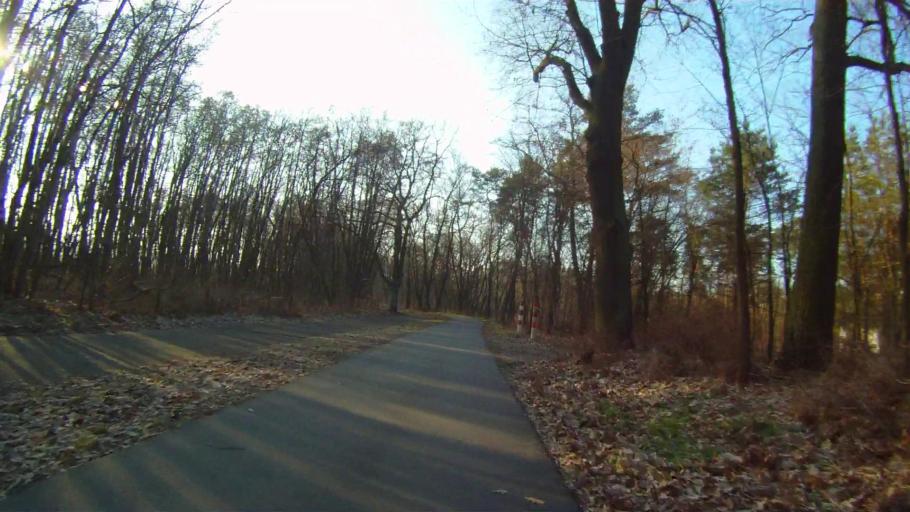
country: DE
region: Berlin
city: Friedrichshagen
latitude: 52.4383
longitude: 13.6203
